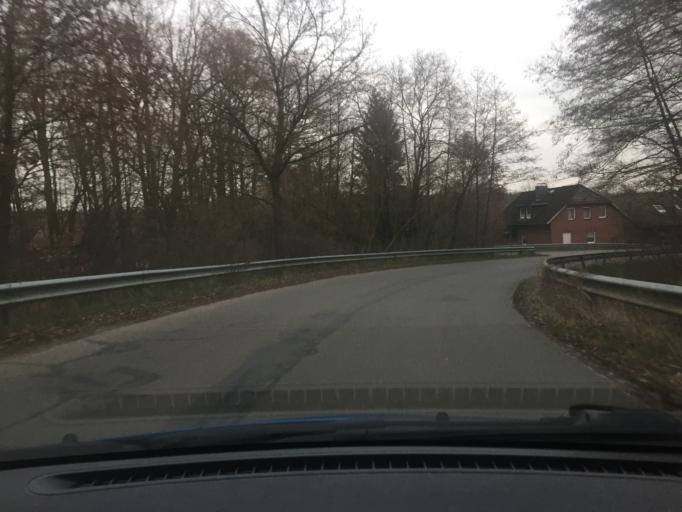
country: DE
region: Lower Saxony
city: Jelmstorf
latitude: 53.1091
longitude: 10.5414
